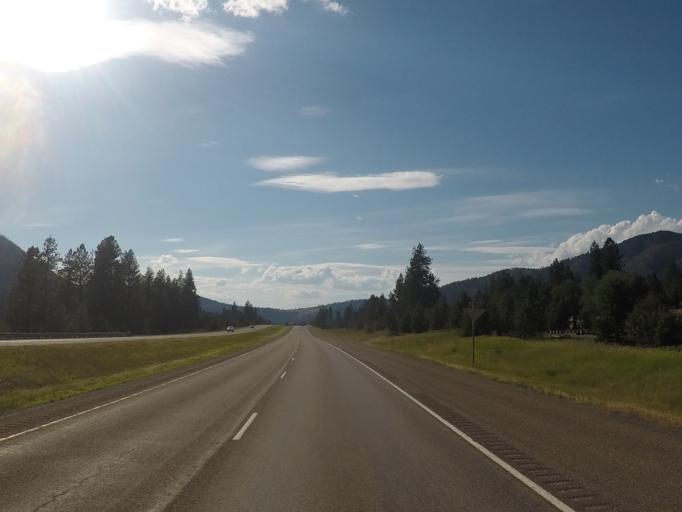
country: US
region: Montana
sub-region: Missoula County
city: Bonner-West Riverside
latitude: 46.8633
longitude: -113.8680
